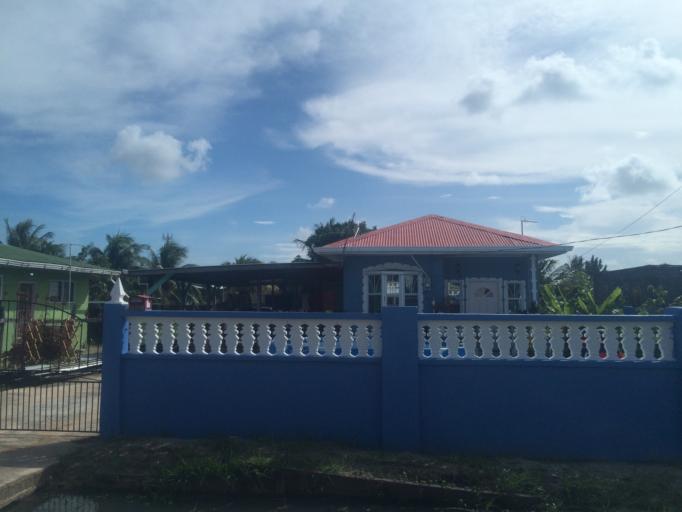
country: GY
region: Demerara-Mahaica
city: Georgetown
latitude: 6.8008
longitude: -58.1292
